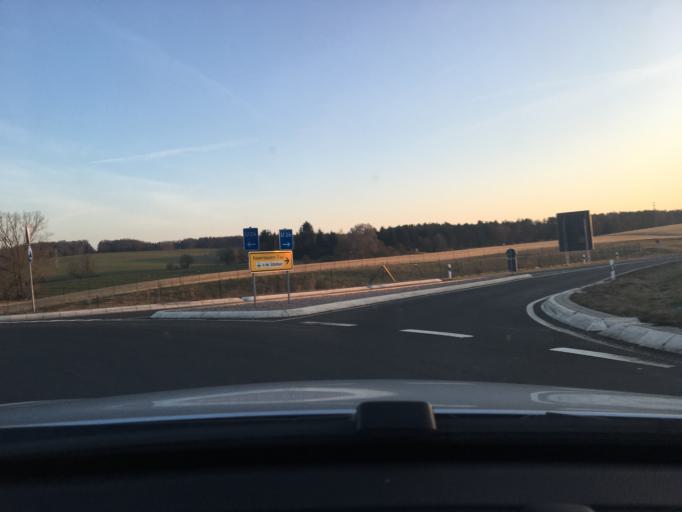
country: DE
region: Rheinland-Pfalz
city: Enkenbach-Alsenborn
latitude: 49.4828
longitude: 7.9014
